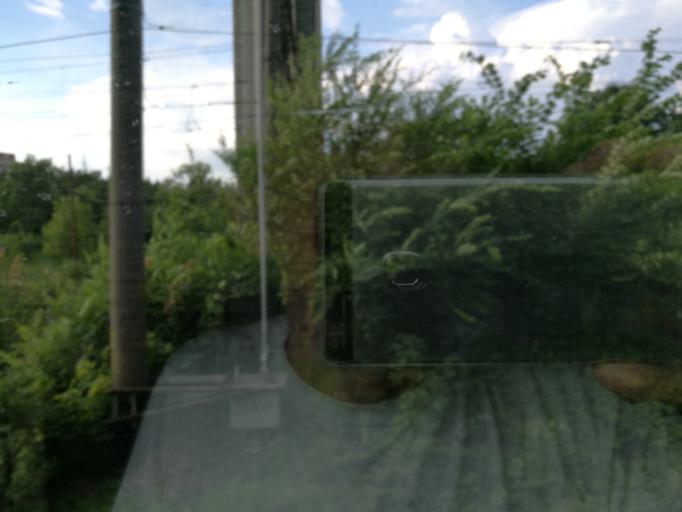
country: RO
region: Brasov
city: Brasov
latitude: 45.6610
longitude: 25.6210
